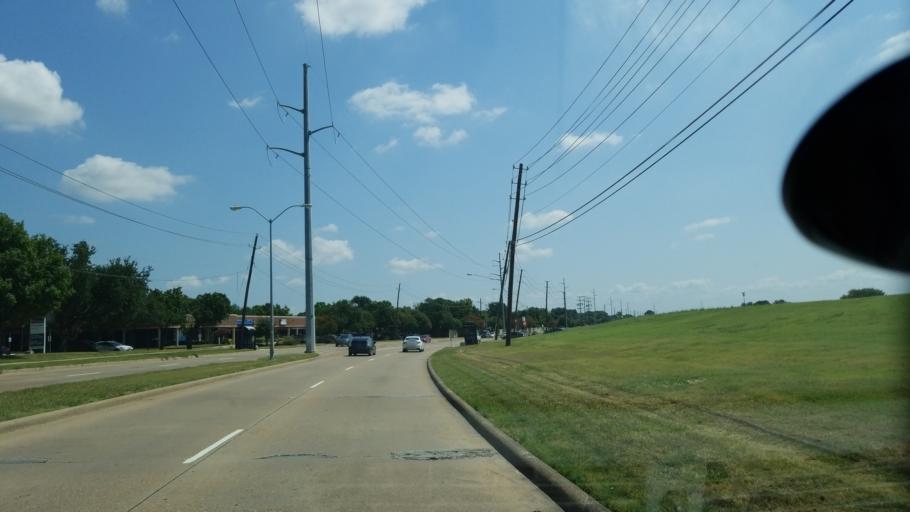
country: US
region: Texas
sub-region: Dallas County
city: Richardson
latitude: 32.9250
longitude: -96.7336
